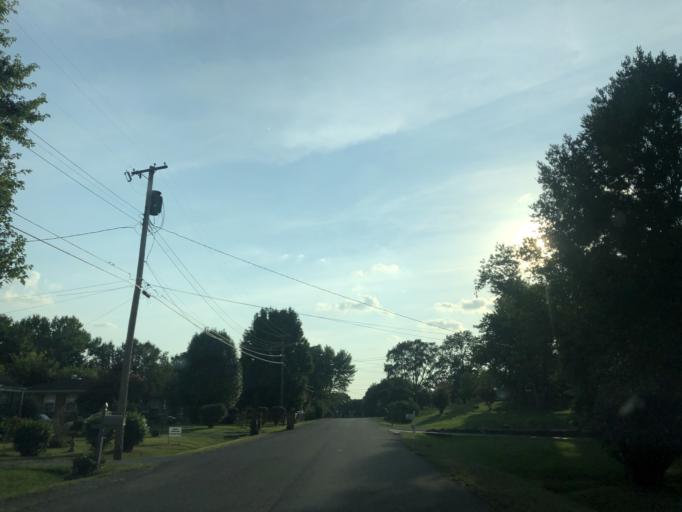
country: US
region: Tennessee
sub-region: Davidson County
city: Nashville
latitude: 36.1535
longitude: -86.6959
